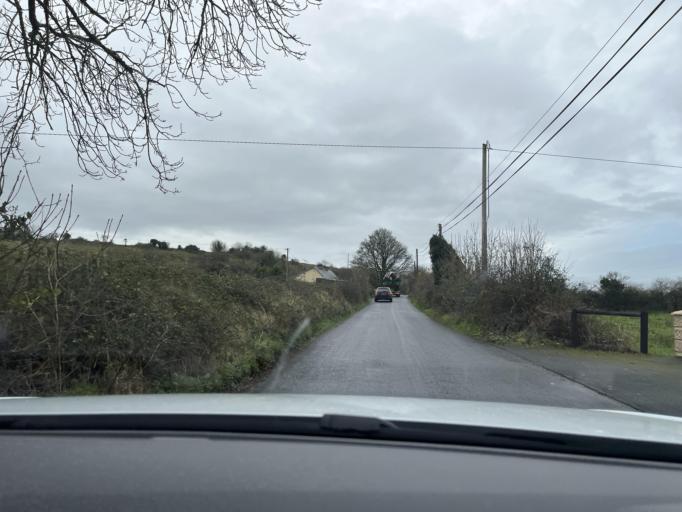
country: IE
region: Connaught
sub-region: County Leitrim
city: Manorhamilton
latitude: 54.2368
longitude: -8.2768
